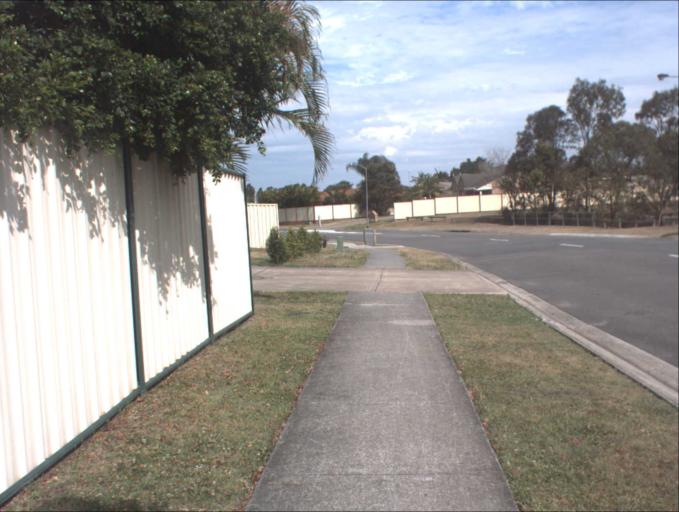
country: AU
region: Queensland
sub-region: Logan
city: Slacks Creek
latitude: -27.6818
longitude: 153.1728
